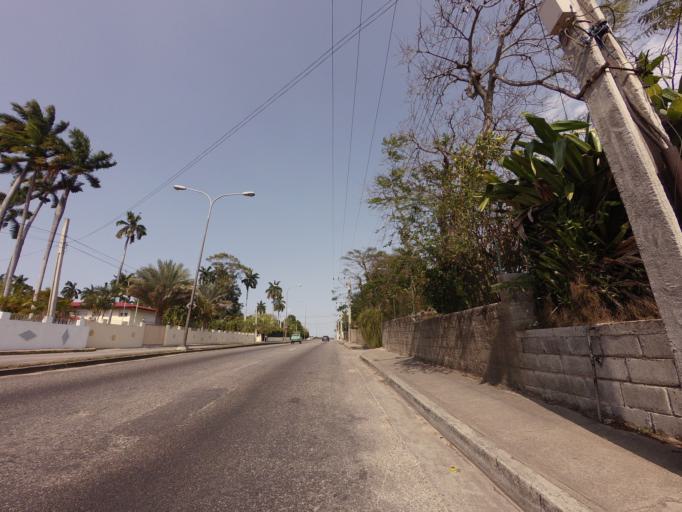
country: CU
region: La Habana
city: Cerro
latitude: 23.0764
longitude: -82.4553
